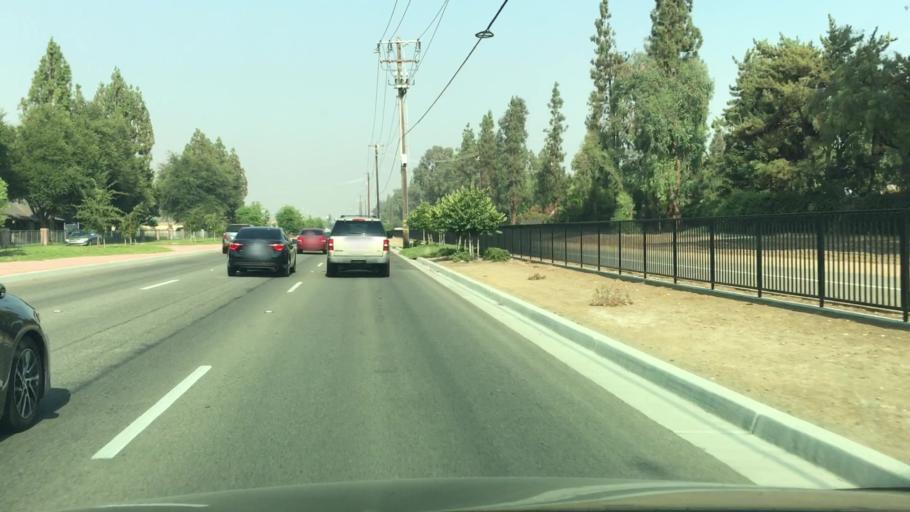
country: US
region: California
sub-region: Fresno County
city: Fresno
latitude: 36.8371
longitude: -119.8591
